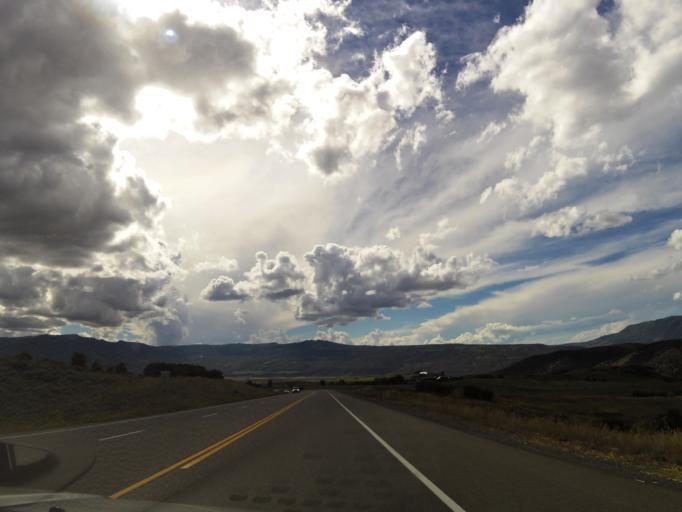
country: US
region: Colorado
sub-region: Hinsdale County
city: Lake City
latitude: 38.3959
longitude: -107.4657
